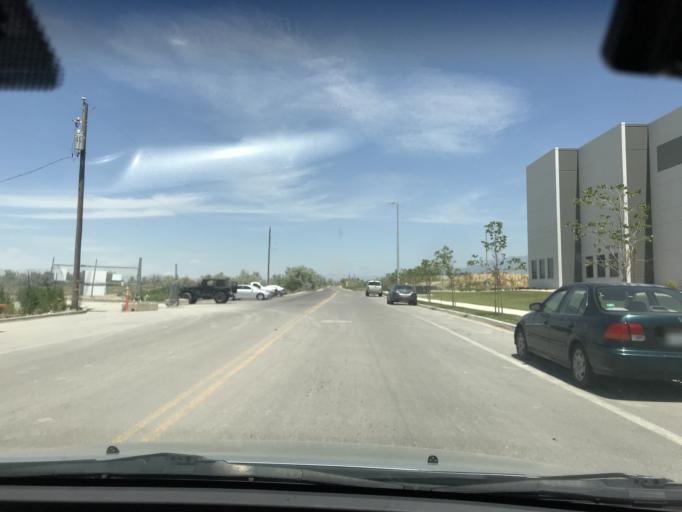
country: US
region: Utah
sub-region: Davis County
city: North Salt Lake
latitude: 40.8159
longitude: -111.9534
